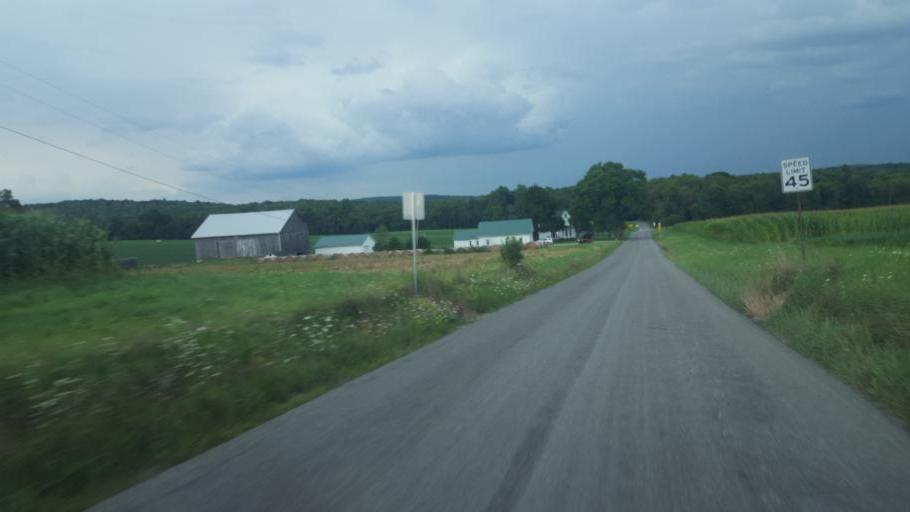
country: US
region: Pennsylvania
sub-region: Clarion County
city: Knox
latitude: 41.1739
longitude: -79.5320
